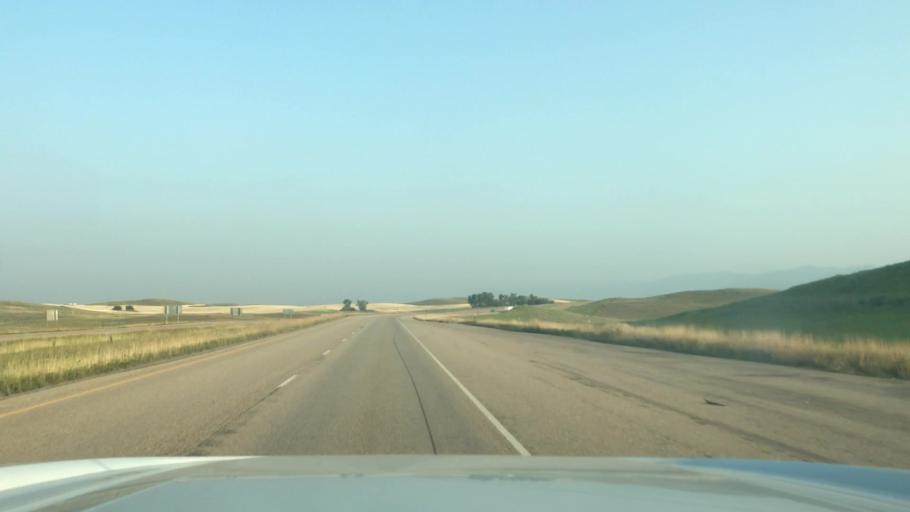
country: US
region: Wyoming
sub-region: Sheridan County
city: Sheridan
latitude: 45.0090
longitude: -107.3016
